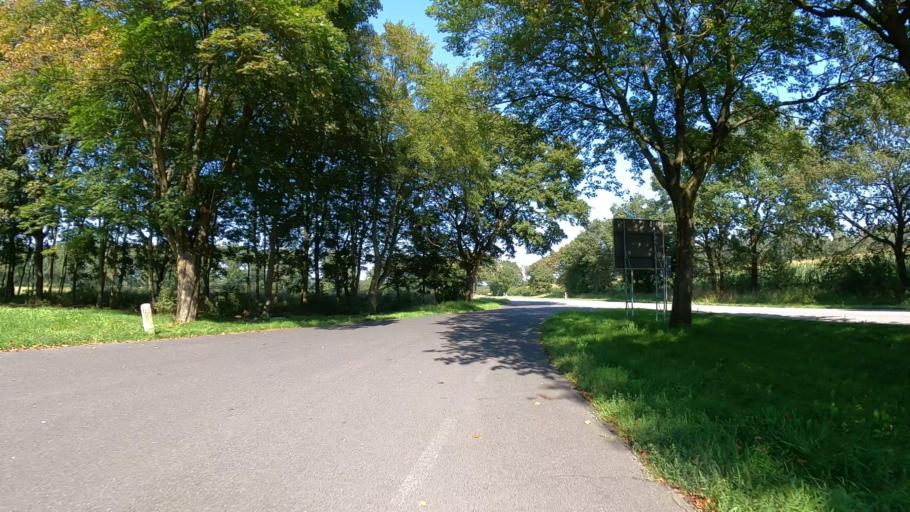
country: DE
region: Schleswig-Holstein
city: Lentfohrden
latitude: 53.8842
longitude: 9.8864
